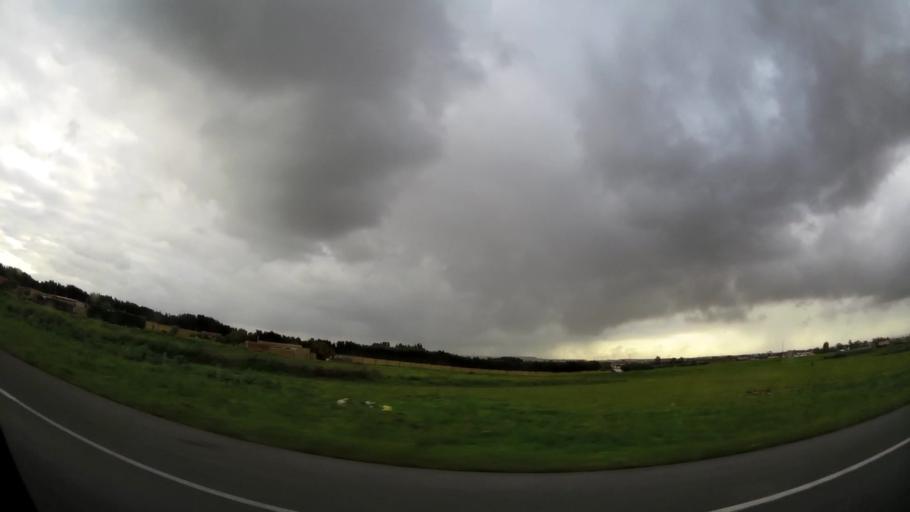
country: MA
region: Grand Casablanca
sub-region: Mediouna
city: Tit Mellil
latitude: 33.5801
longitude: -7.4529
